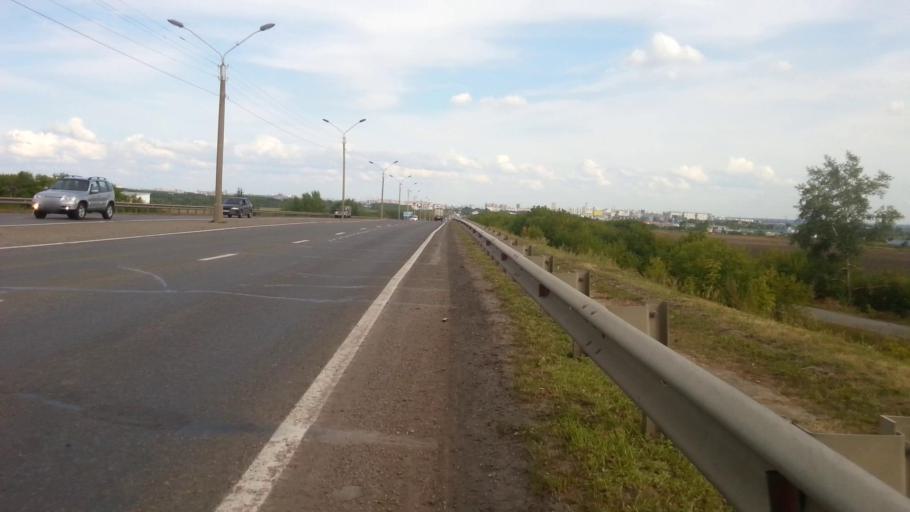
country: RU
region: Altai Krai
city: Novosilikatnyy
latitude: 53.3513
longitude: 83.5877
